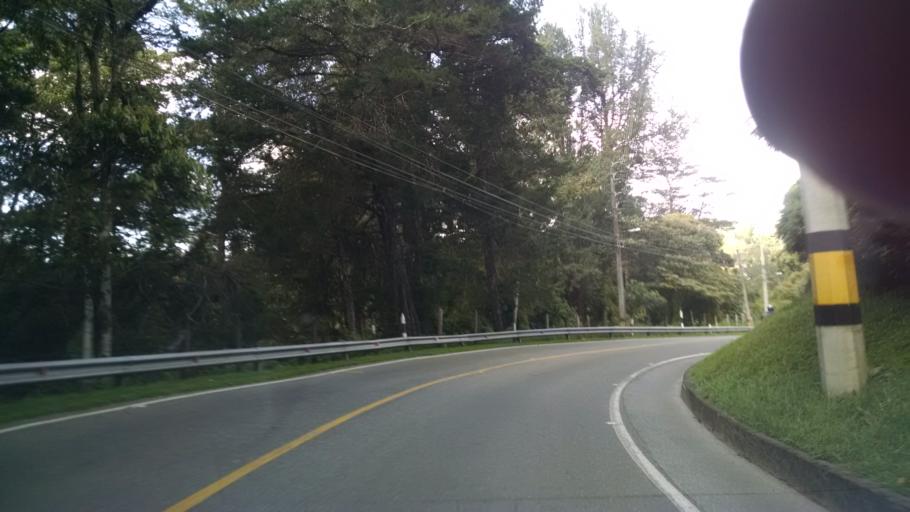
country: CO
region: Antioquia
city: El Retiro
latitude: 6.0858
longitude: -75.4931
